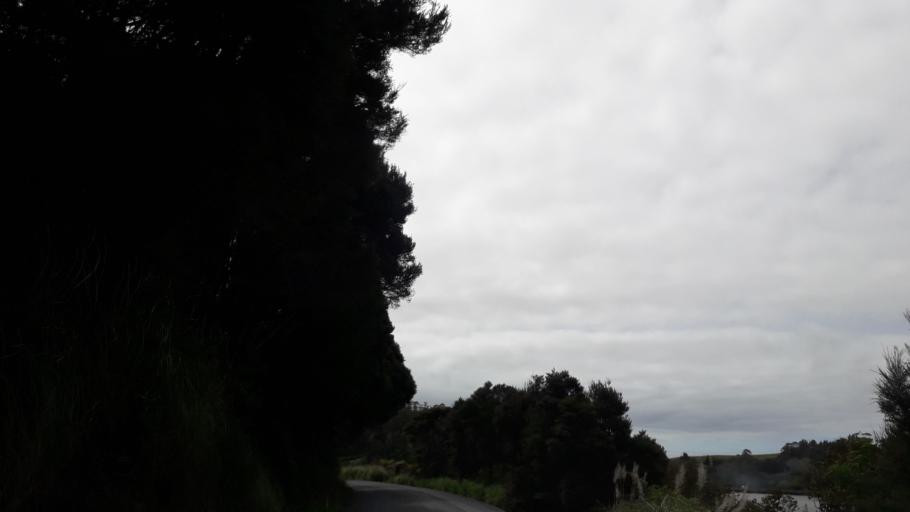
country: NZ
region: Northland
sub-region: Far North District
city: Taipa
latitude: -35.0174
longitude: 173.5506
